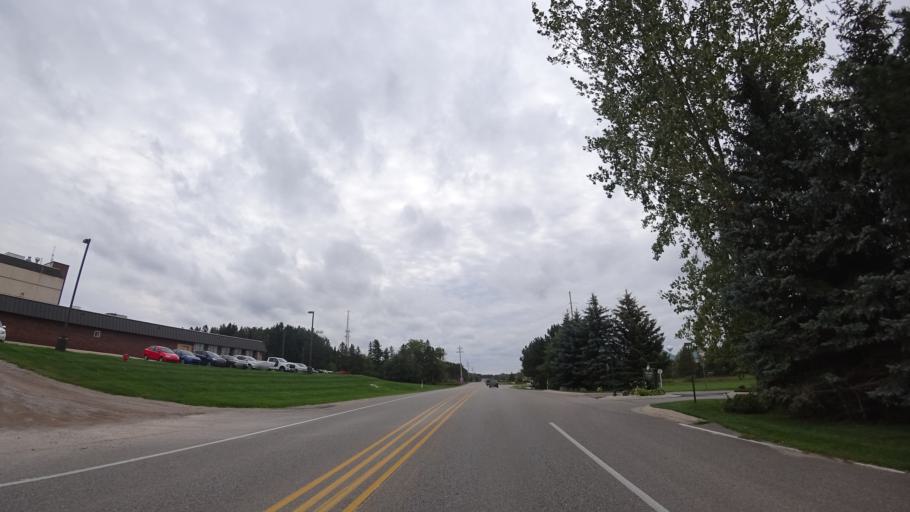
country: US
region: Michigan
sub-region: Emmet County
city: Petoskey
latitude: 45.3565
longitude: -84.9709
